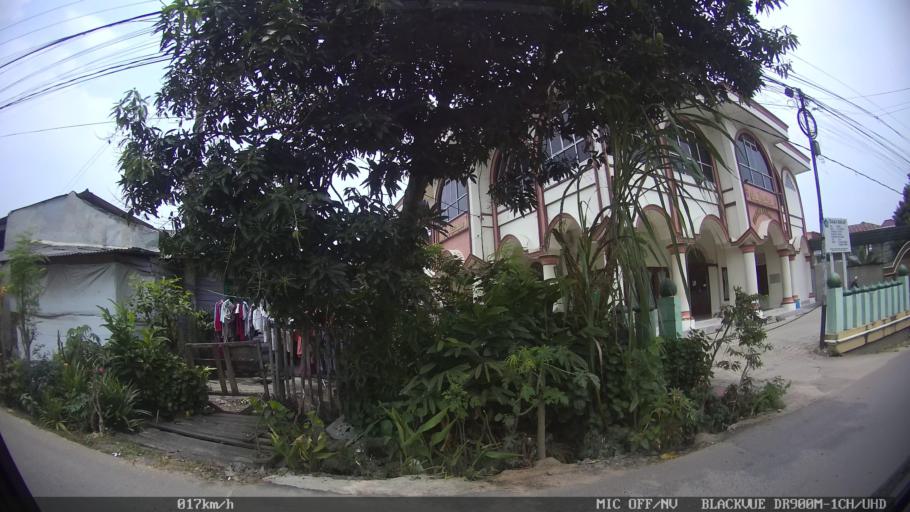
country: ID
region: Lampung
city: Kedaton
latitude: -5.3932
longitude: 105.3006
